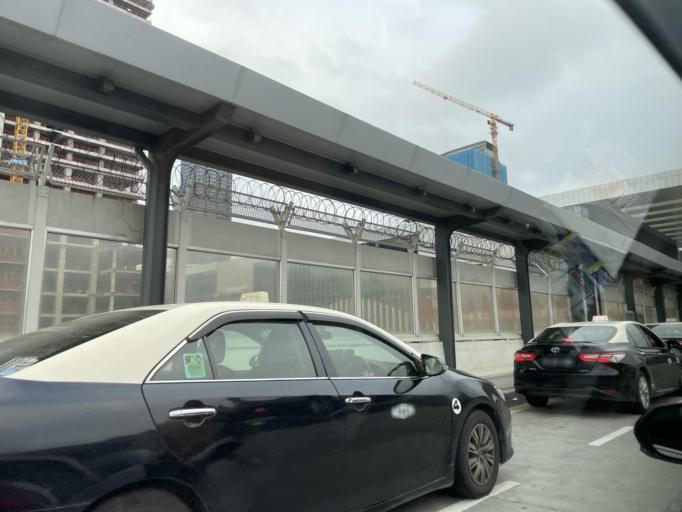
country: MO
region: Macau
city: Macau
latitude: 22.1391
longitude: 113.5452
